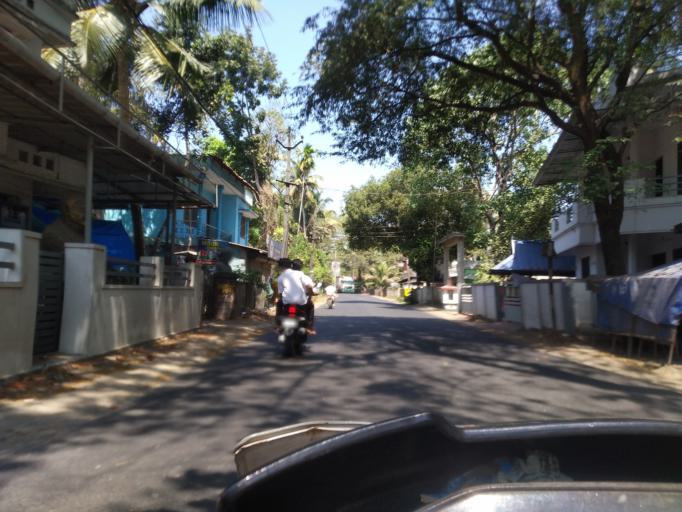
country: IN
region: Kerala
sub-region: Thrissur District
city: Kodungallur
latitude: 10.1745
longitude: 76.2118
